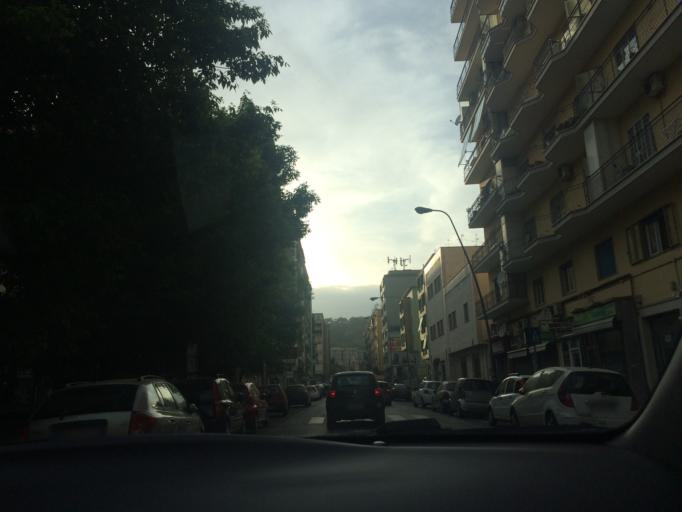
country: IT
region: Campania
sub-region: Provincia di Napoli
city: Bagnoli
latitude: 40.8301
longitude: 14.1958
